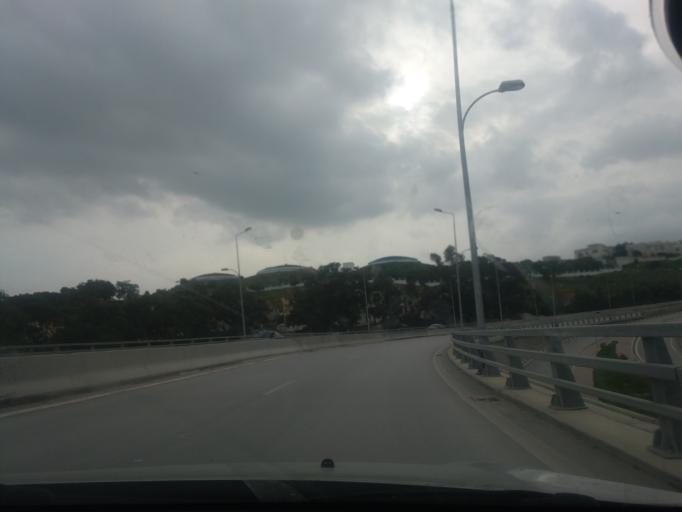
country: TN
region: Ariana
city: Ariana
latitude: 36.8663
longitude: 10.1834
